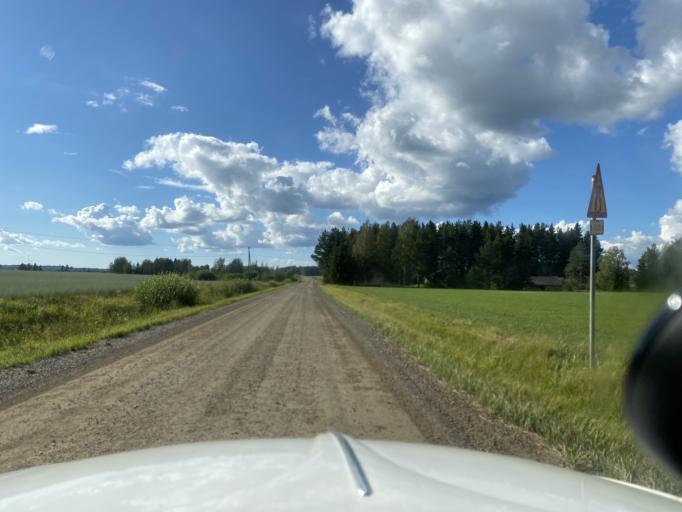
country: FI
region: Pirkanmaa
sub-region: Lounais-Pirkanmaa
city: Punkalaidun
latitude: 61.1308
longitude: 23.2390
